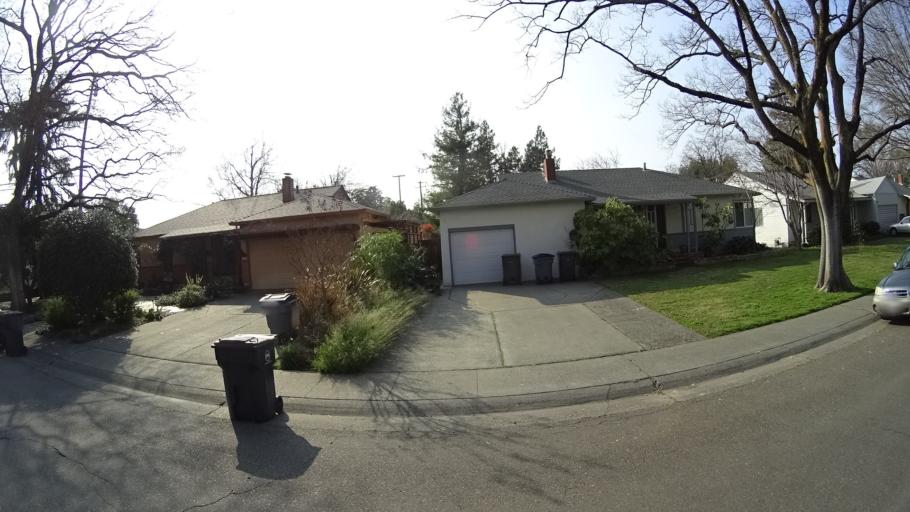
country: US
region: California
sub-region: Yolo County
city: Davis
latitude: 38.5495
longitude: -121.7383
